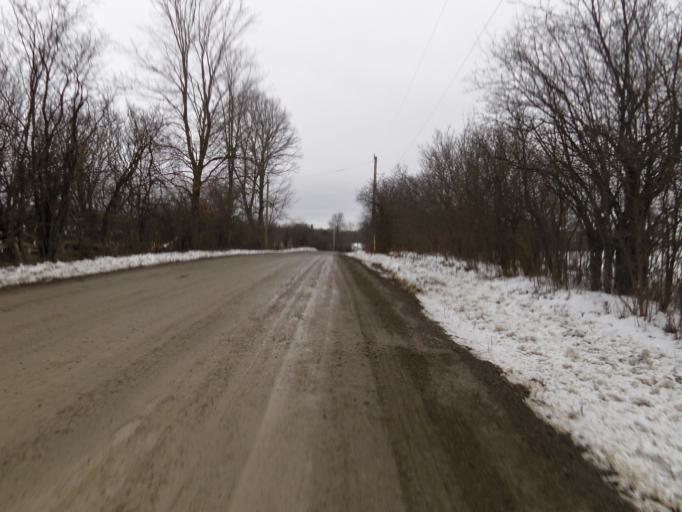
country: CA
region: Ontario
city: Carleton Place
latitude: 45.1981
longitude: -76.2145
